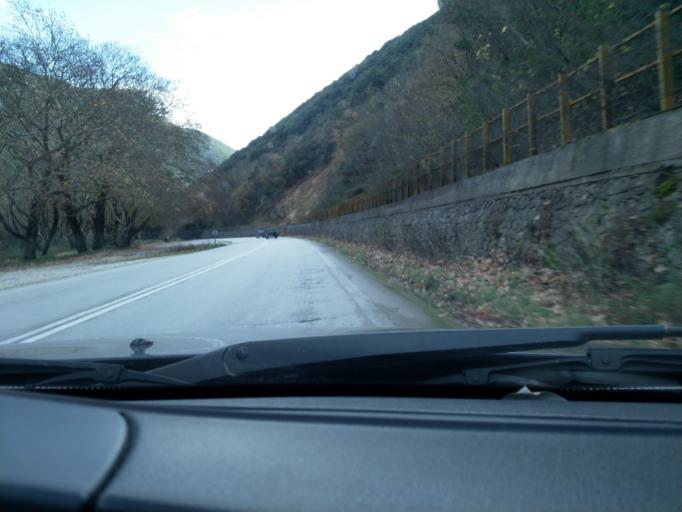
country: GR
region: Epirus
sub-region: Nomos Prevezis
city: Pappadates
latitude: 39.3966
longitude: 20.8447
